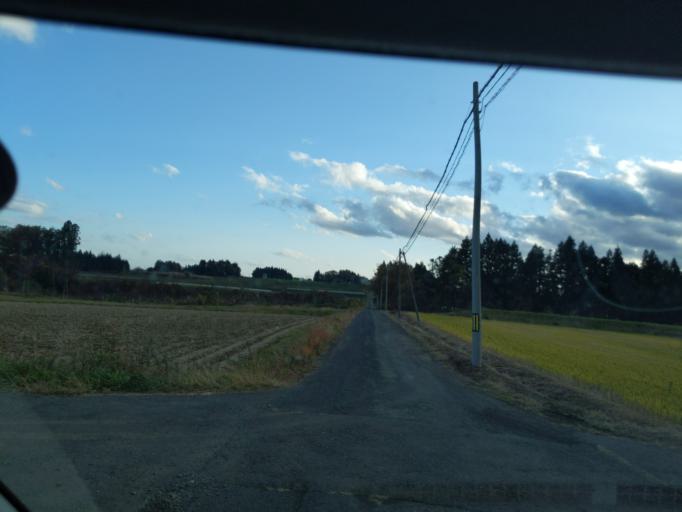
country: JP
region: Iwate
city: Mizusawa
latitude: 39.0978
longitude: 141.0392
